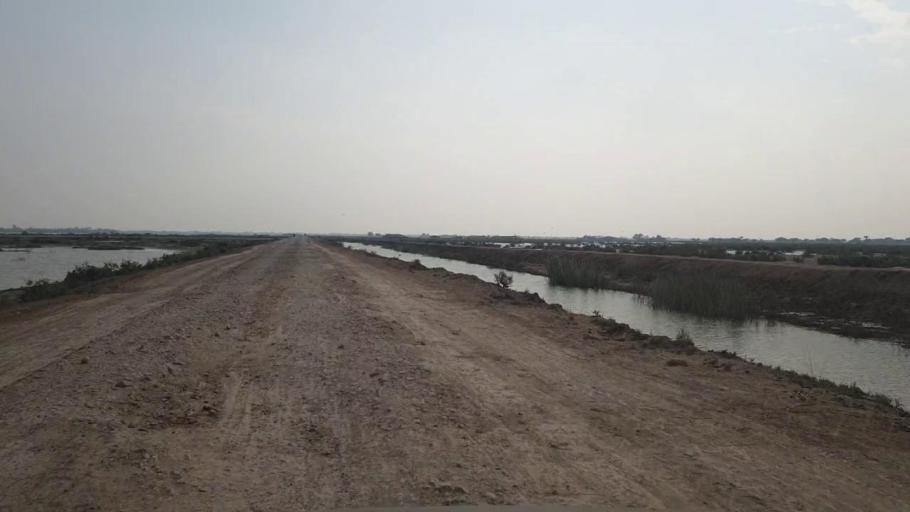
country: PK
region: Sindh
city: Tando Muhammad Khan
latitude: 25.0916
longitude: 68.3831
